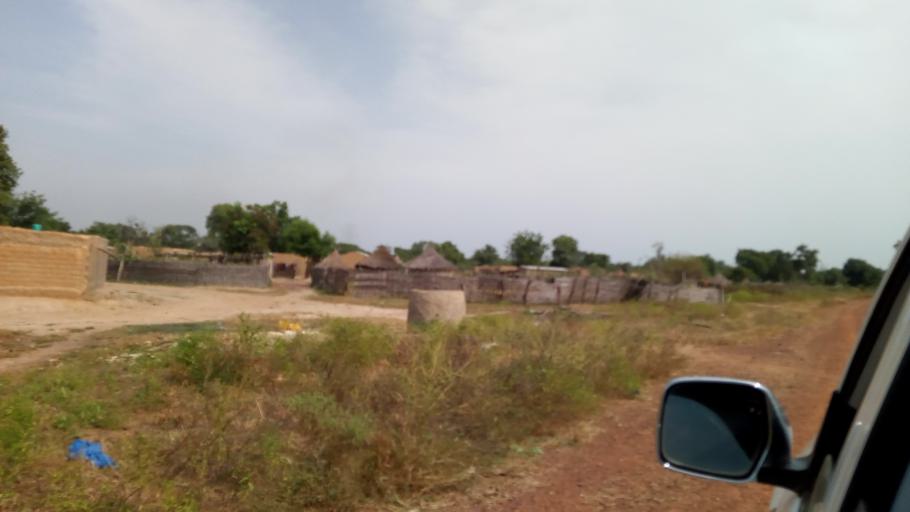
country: ML
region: Kayes
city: Kita
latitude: 13.2613
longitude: -8.8552
